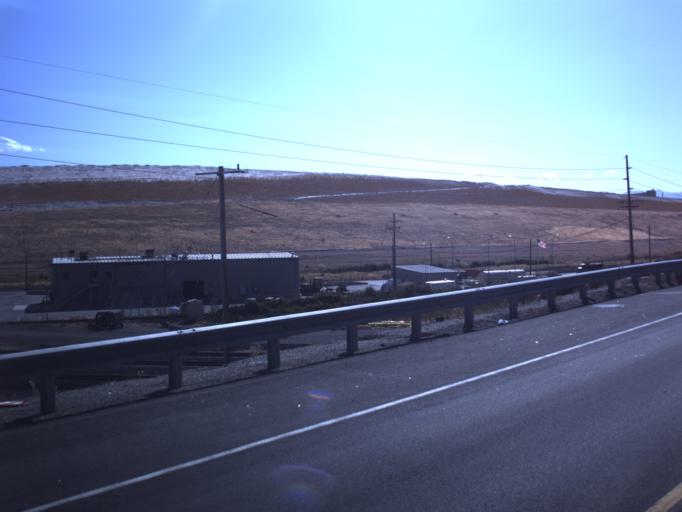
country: US
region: Utah
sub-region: Salt Lake County
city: Magna
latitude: 40.7415
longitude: -112.1785
